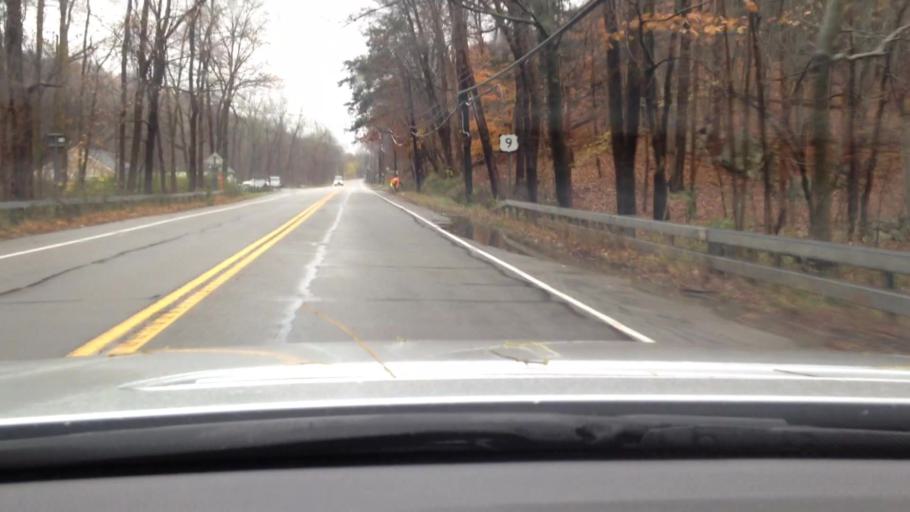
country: US
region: New York
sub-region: Westchester County
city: Peekskill
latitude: 41.3260
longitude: -73.9280
